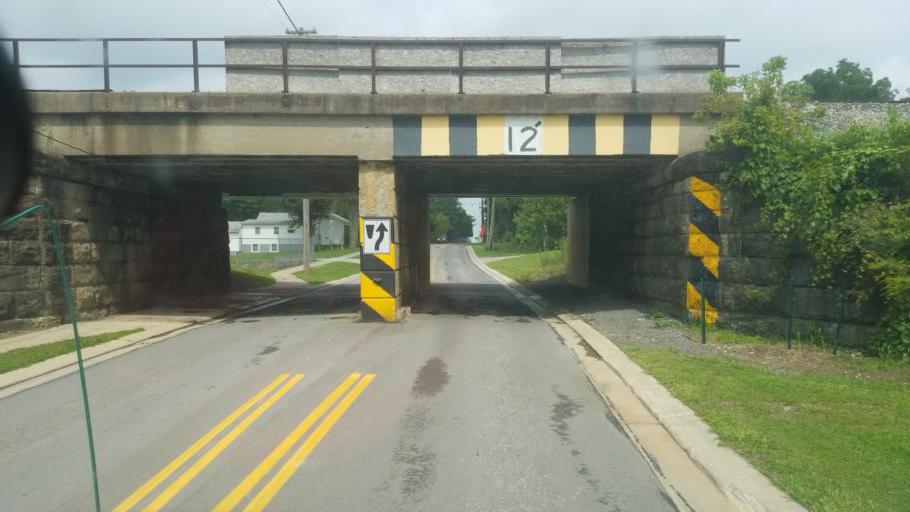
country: US
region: Ohio
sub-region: Huron County
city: Greenwich
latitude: 41.0347
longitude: -82.5165
